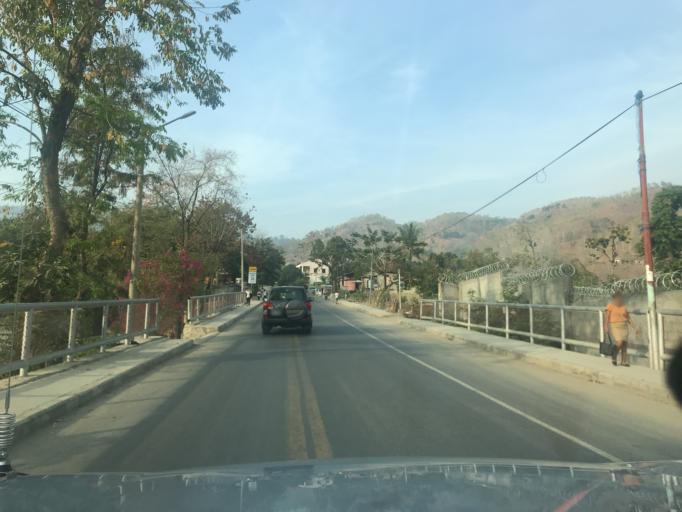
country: TL
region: Dili
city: Dili
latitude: -8.5697
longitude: 125.5840
